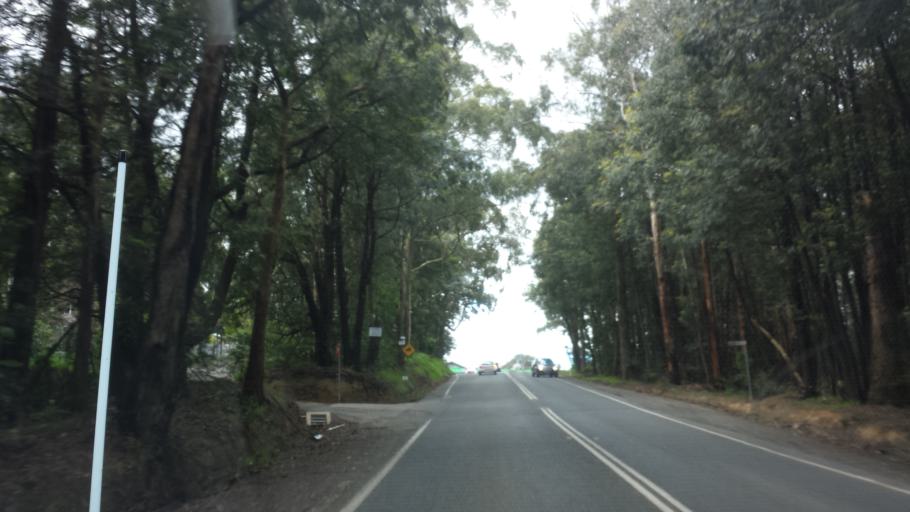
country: AU
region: Victoria
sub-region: Cardinia
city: Emerald
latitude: -37.9303
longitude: 145.4217
